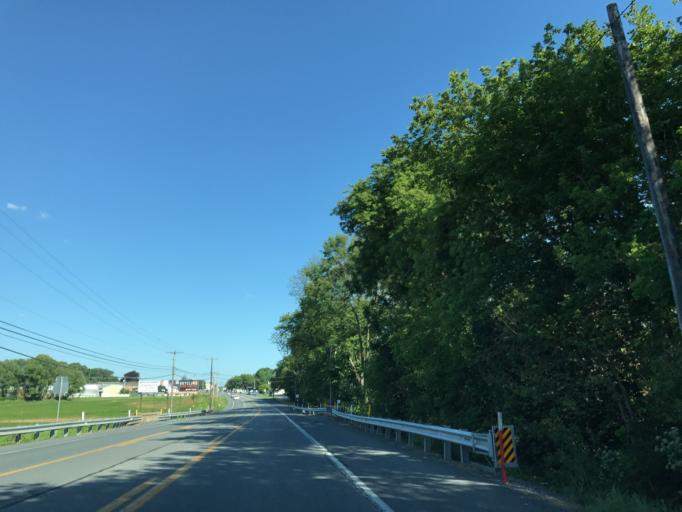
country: US
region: Pennsylvania
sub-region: Lancaster County
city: Rheems
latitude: 40.1199
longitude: -76.5392
